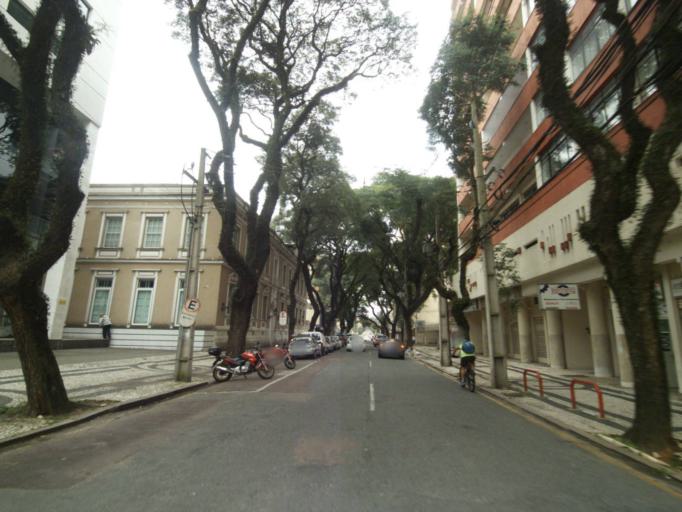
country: BR
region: Parana
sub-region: Curitiba
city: Curitiba
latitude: -25.4329
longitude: -49.2798
